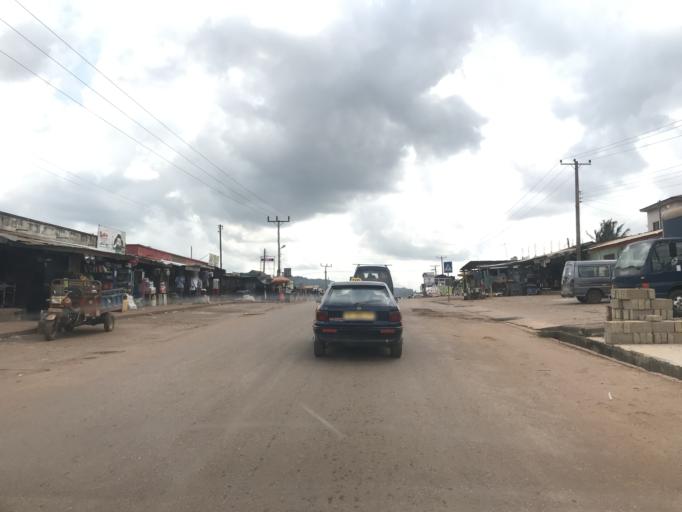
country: GH
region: Ashanti
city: Obuasi
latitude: 6.1984
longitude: -1.6355
